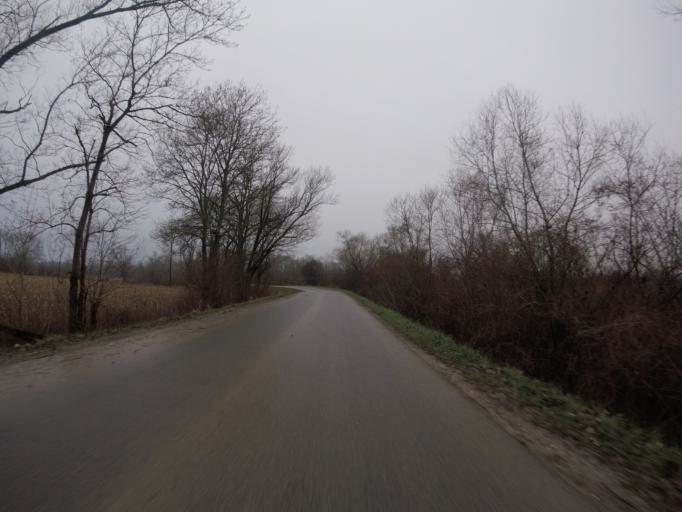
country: HR
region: Sisacko-Moslavacka
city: Lekenik
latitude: 45.6255
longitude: 16.3209
